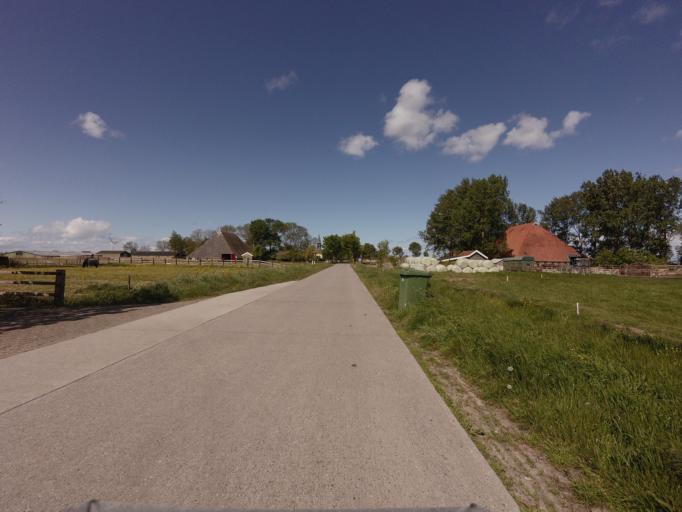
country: NL
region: Friesland
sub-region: Sudwest Fryslan
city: Workum
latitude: 53.0063
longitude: 5.4366
